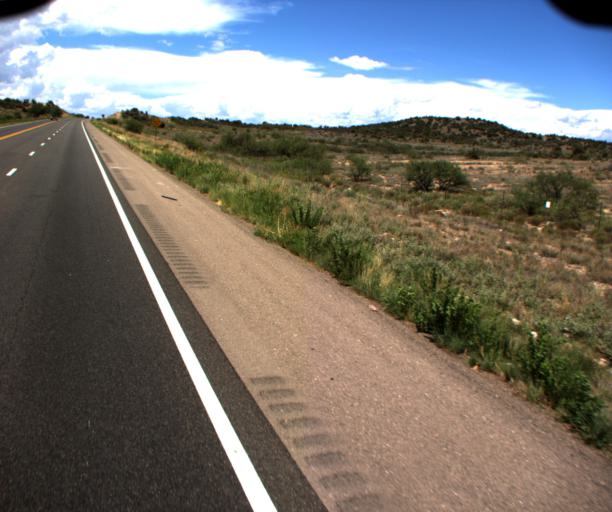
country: US
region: Arizona
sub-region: Yavapai County
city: Cornville
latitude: 34.6447
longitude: -111.9508
